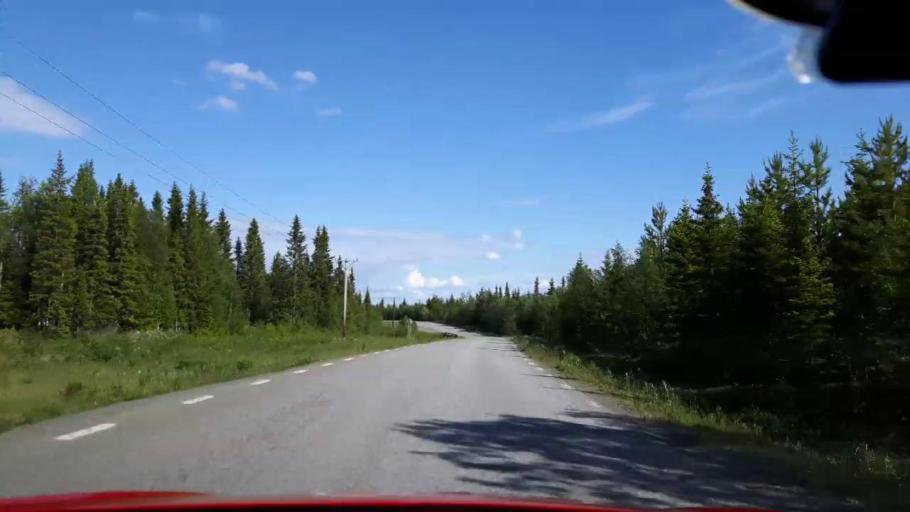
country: SE
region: Jaemtland
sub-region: Krokoms Kommun
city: Valla
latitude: 63.6938
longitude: 14.2065
